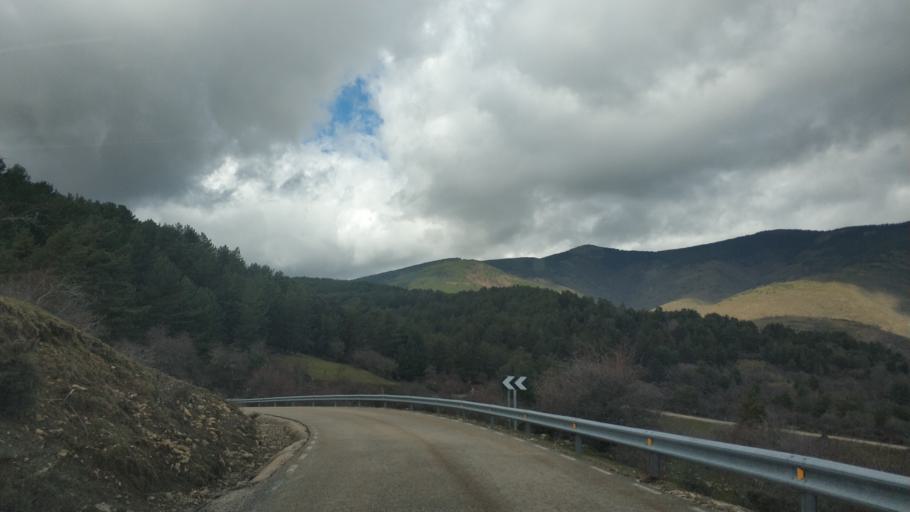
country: ES
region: Castille and Leon
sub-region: Provincia de Burgos
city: Neila
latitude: 42.0546
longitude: -3.0099
